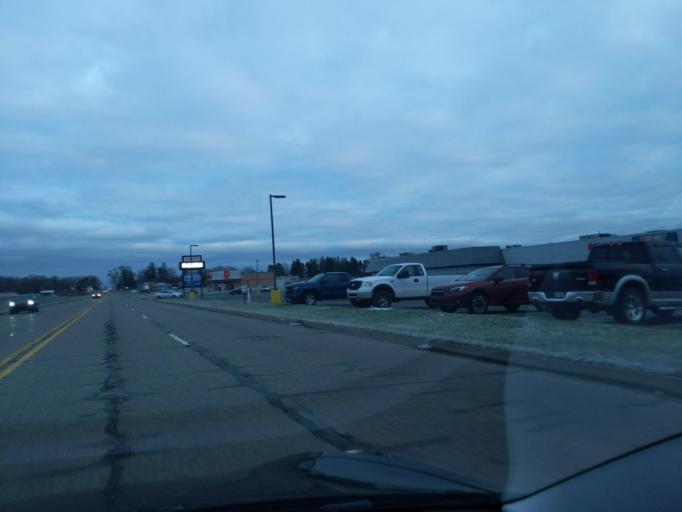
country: US
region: Michigan
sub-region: Jackson County
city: Jackson
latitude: 42.2547
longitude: -84.4574
